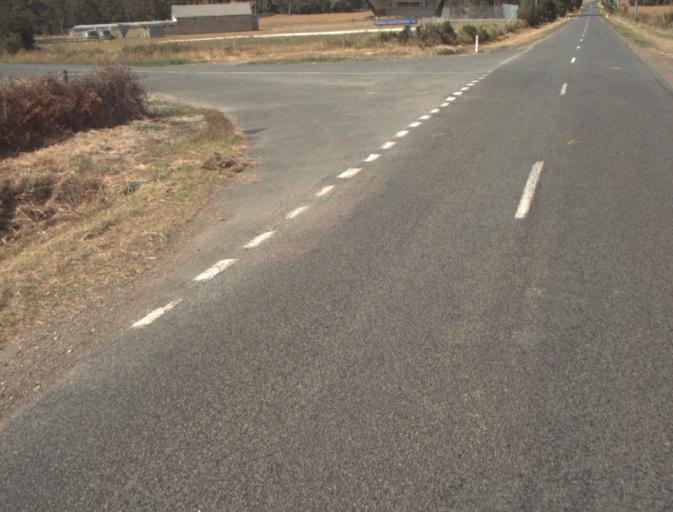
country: AU
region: Tasmania
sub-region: Launceston
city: Mayfield
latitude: -41.2524
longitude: 147.1473
